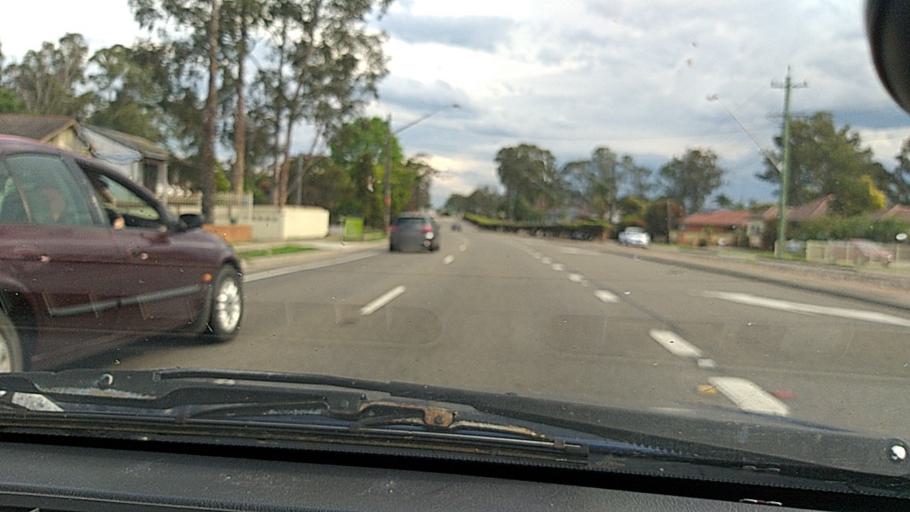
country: AU
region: New South Wales
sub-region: Penrith Municipality
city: Cambridge Park
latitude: -33.7445
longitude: 150.7150
